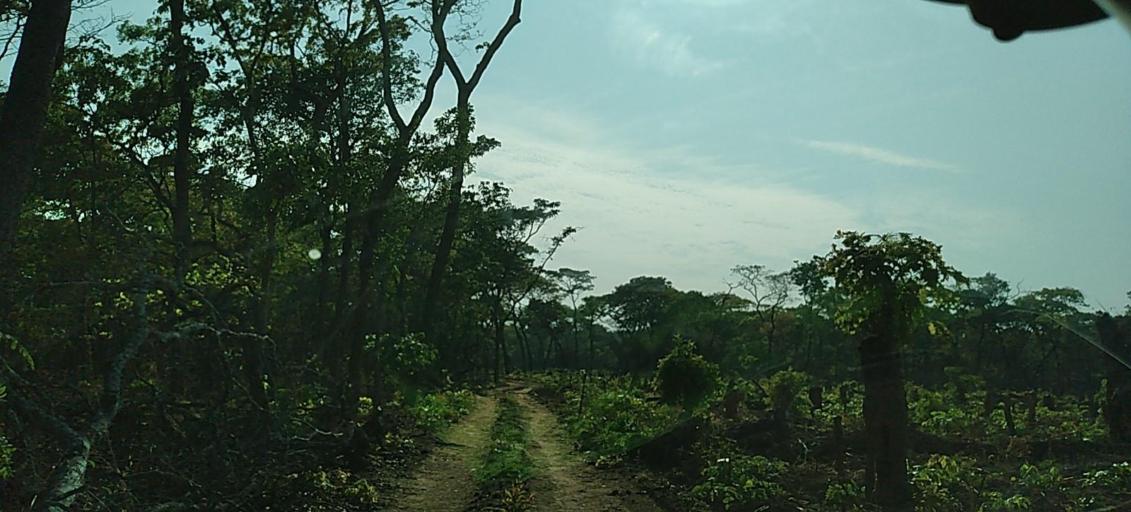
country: ZM
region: North-Western
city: Kalengwa
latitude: -13.2339
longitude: 25.0685
